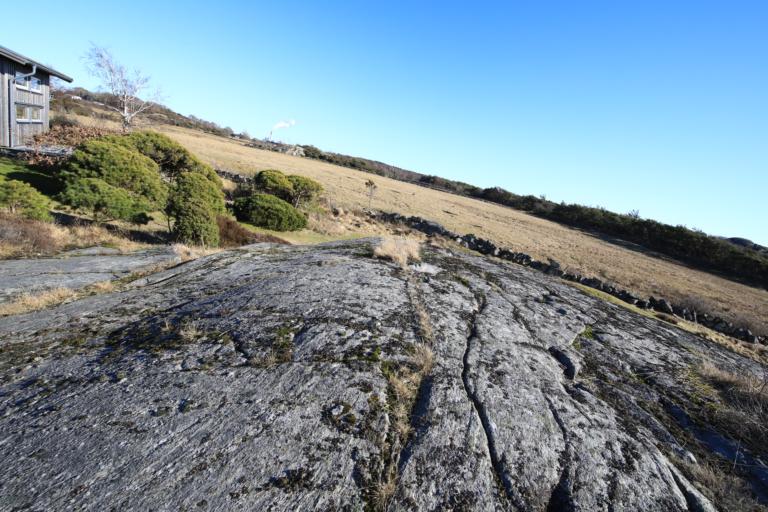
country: SE
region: Halland
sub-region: Kungsbacka Kommun
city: Frillesas
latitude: 57.2268
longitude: 12.1257
